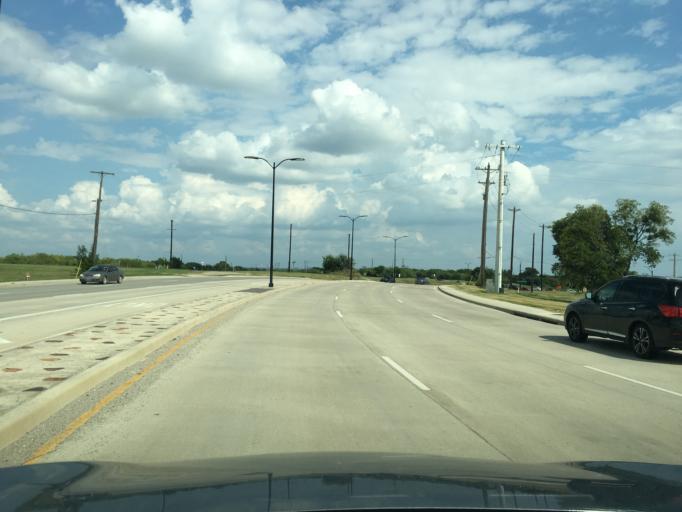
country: US
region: Texas
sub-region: Denton County
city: Little Elm
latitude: 33.1644
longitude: -96.9665
